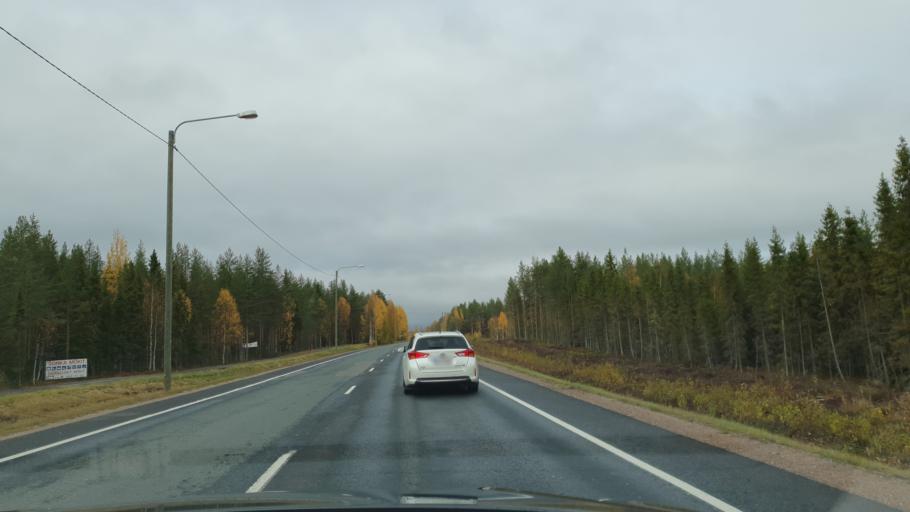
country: FI
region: Lapland
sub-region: Rovaniemi
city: Rovaniemi
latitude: 66.6379
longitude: 25.4936
